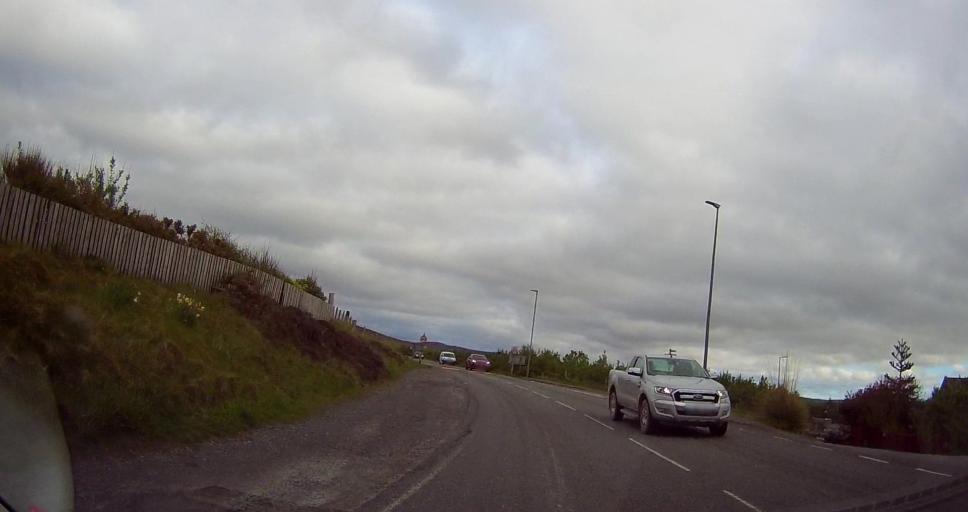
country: GB
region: Scotland
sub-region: Shetland Islands
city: Lerwick
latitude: 60.3881
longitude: -1.3483
